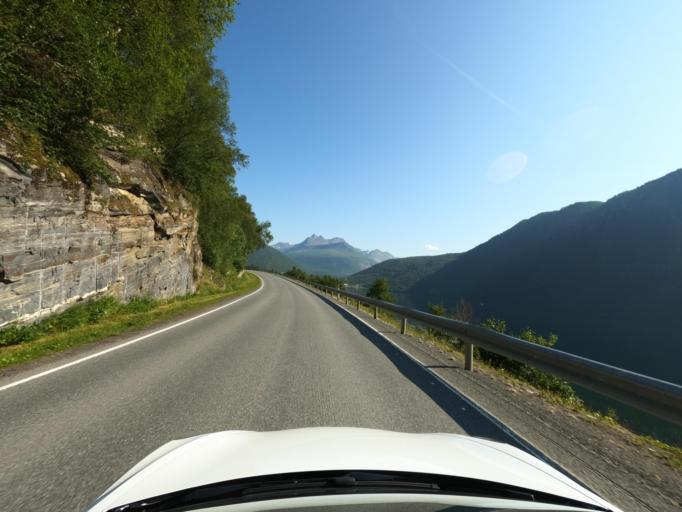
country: NO
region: Nordland
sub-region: Narvik
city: Narvik
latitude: 68.3884
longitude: 17.5506
